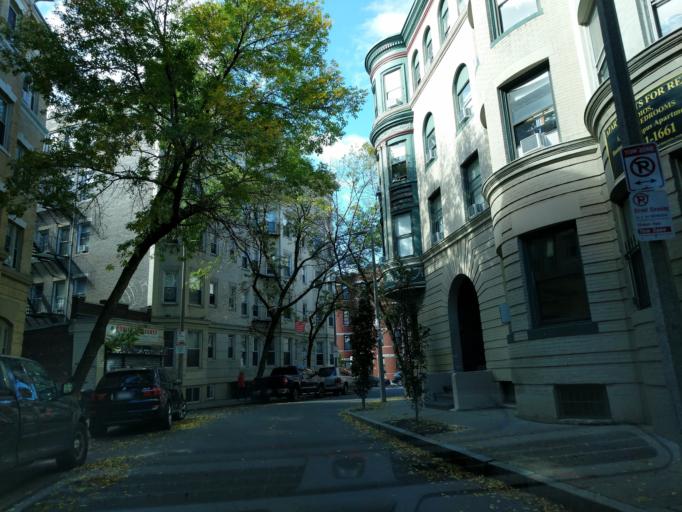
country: US
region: Massachusetts
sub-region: Suffolk County
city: Boston
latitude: 42.3463
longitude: -71.0886
